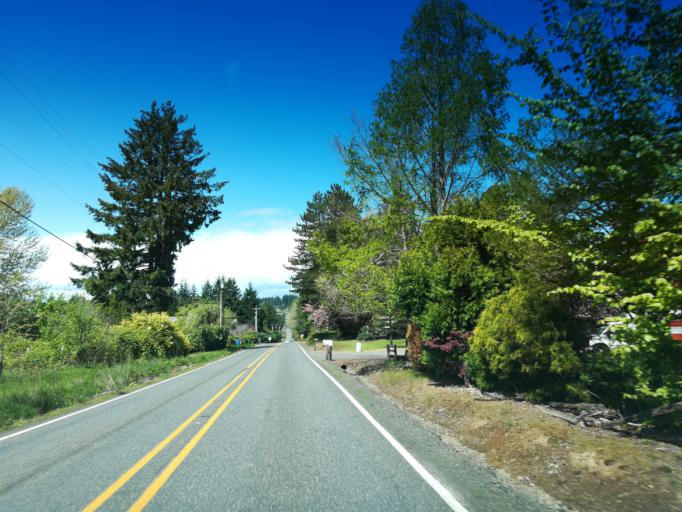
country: US
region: Oregon
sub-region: Clackamas County
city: Damascus
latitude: 45.4363
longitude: -122.4345
